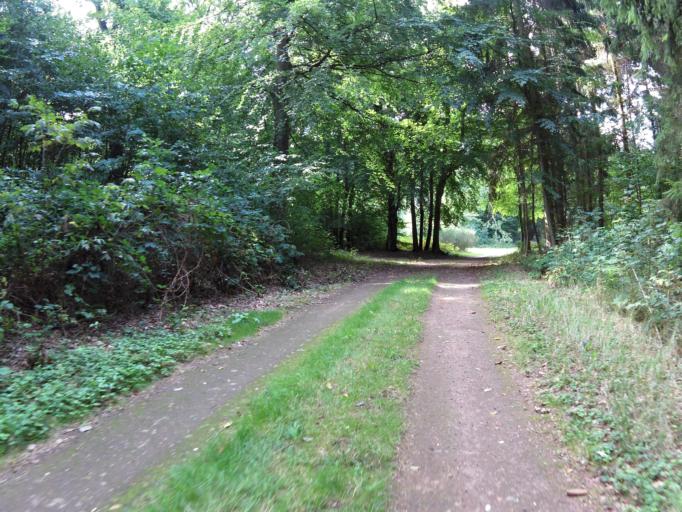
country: DE
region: Mecklenburg-Vorpommern
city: Seebad Bansin
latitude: 53.9491
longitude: 14.1030
